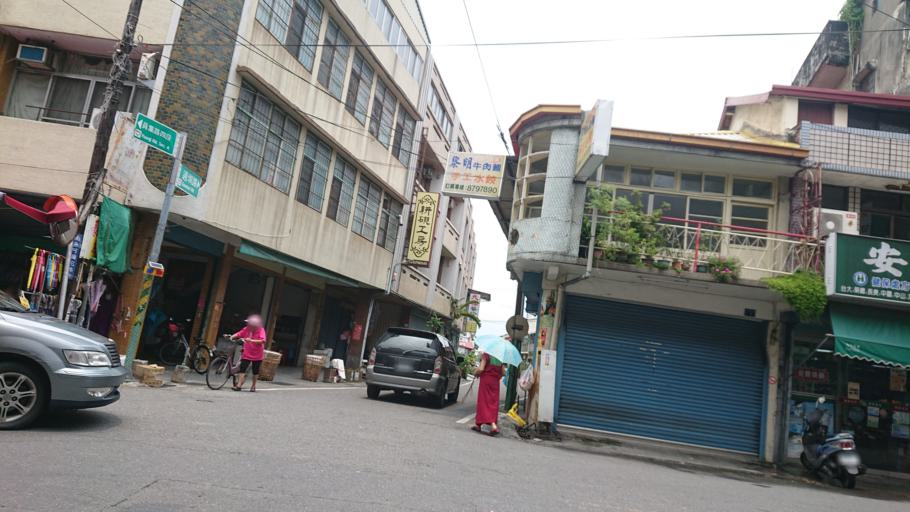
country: TW
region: Taiwan
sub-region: Nantou
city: Nantou
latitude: 23.8113
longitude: 120.6160
